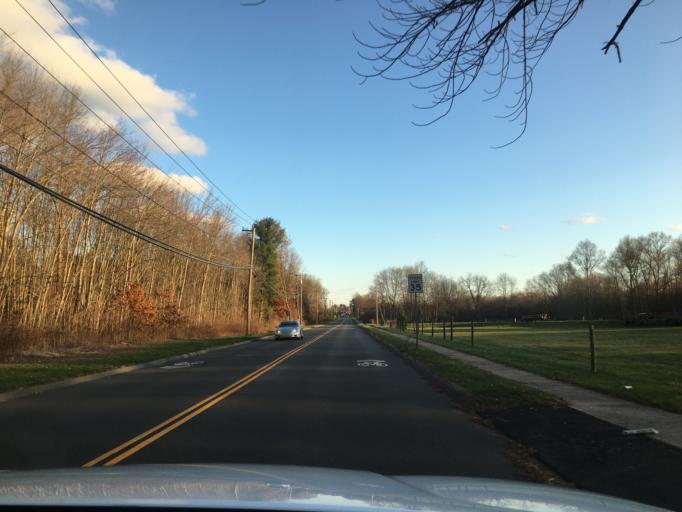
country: US
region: Connecticut
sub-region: Hartford County
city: Enfield
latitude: 41.9676
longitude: -72.5848
